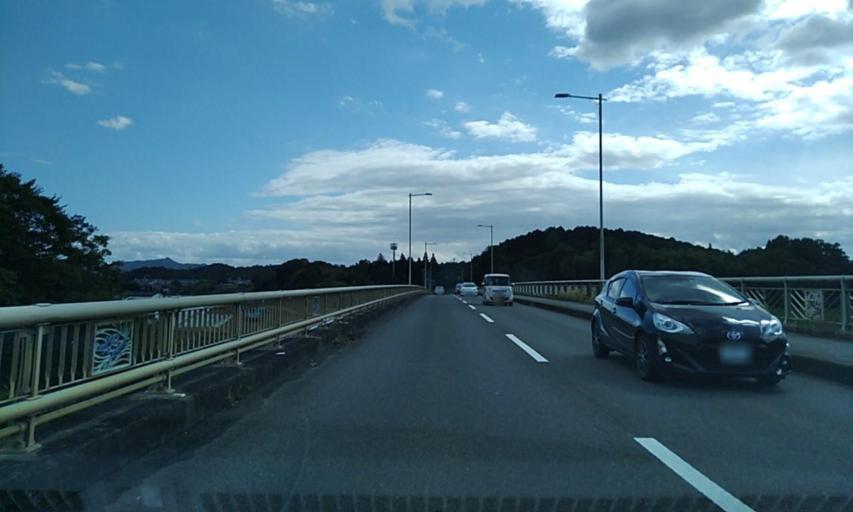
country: JP
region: Kyoto
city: Fukuchiyama
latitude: 35.3041
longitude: 135.1431
